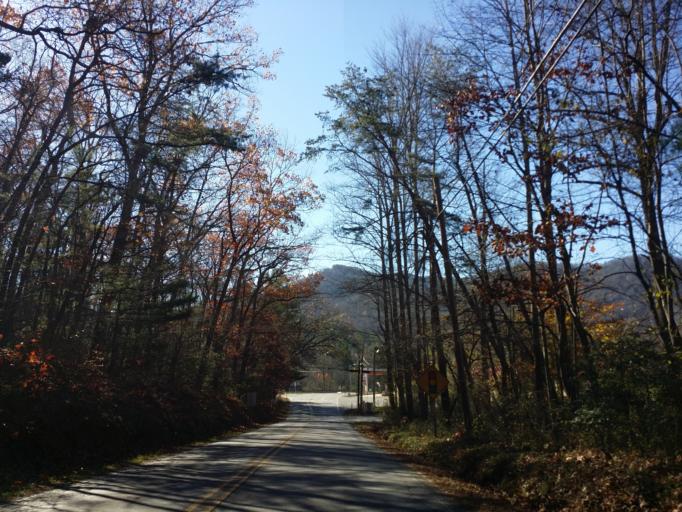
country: US
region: North Carolina
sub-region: Buncombe County
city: Swannanoa
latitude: 35.5946
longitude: -82.4359
